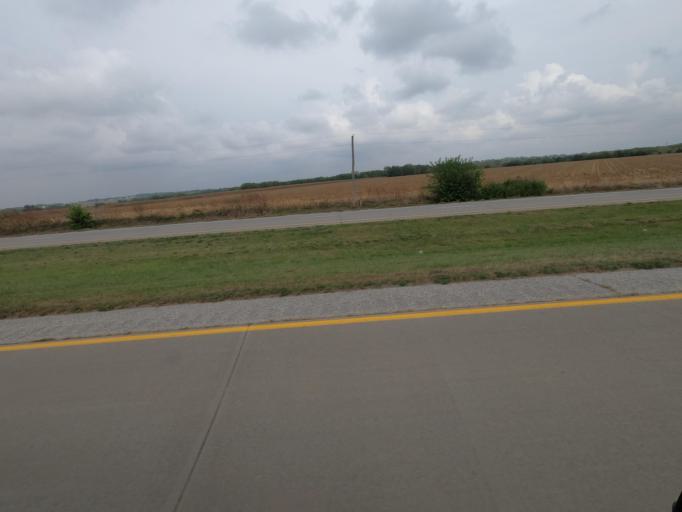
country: US
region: Iowa
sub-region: Wapello County
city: Eddyville
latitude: 41.1238
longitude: -92.5616
